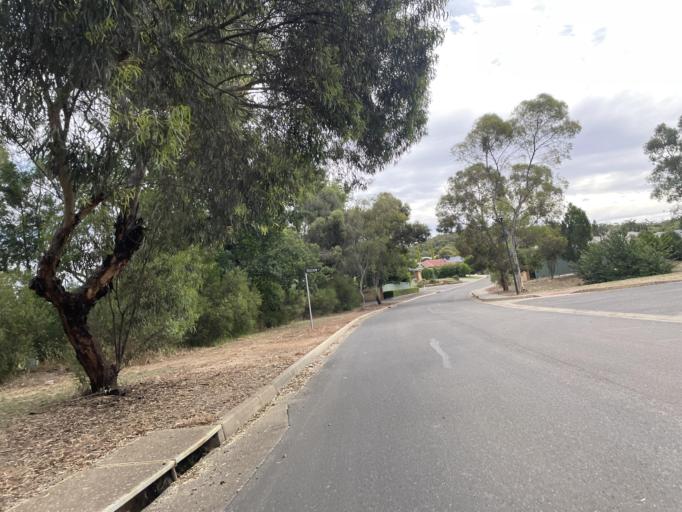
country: AU
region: South Australia
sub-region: Clare and Gilbert Valleys
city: Clare
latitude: -33.8440
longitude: 138.6131
